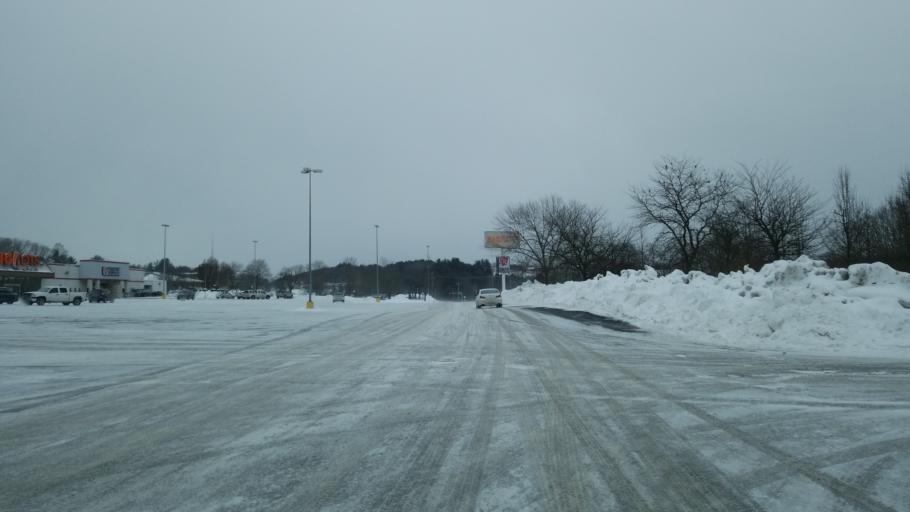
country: US
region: Pennsylvania
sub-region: Clearfield County
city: Clearfield
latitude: 41.0282
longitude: -78.4142
